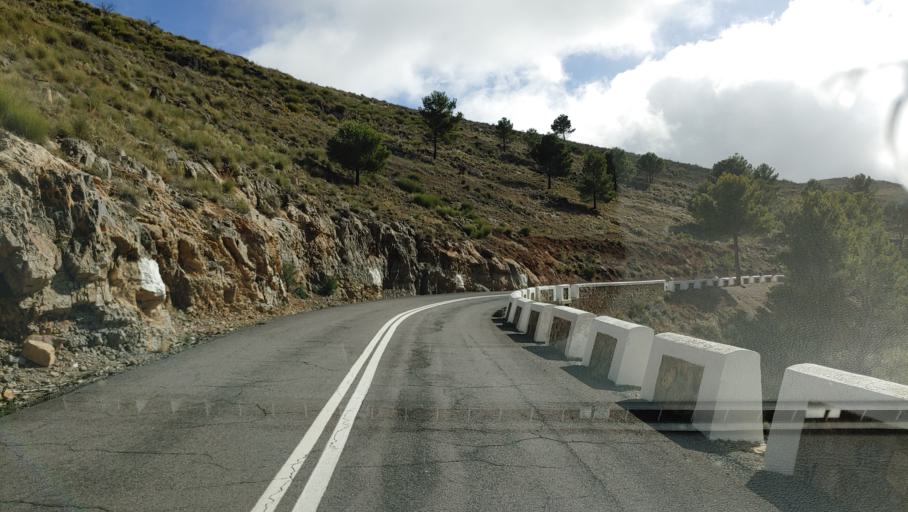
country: ES
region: Andalusia
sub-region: Provincia de Almeria
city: Enix
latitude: 36.9166
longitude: -2.6010
